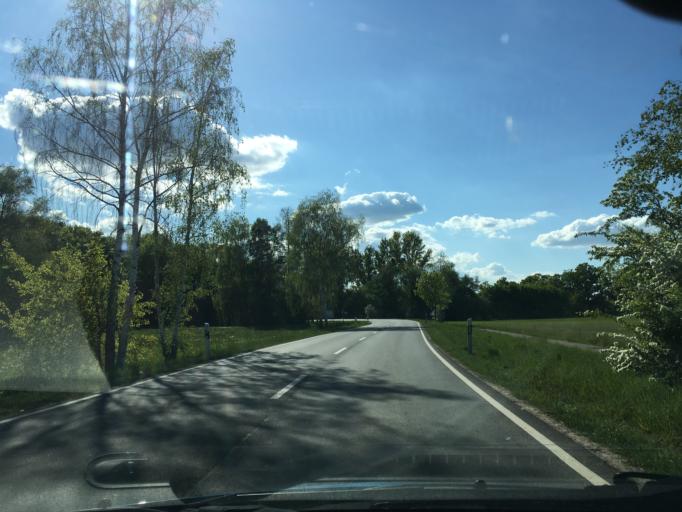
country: DE
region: Lower Saxony
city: Gartow
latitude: 53.0271
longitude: 11.4736
